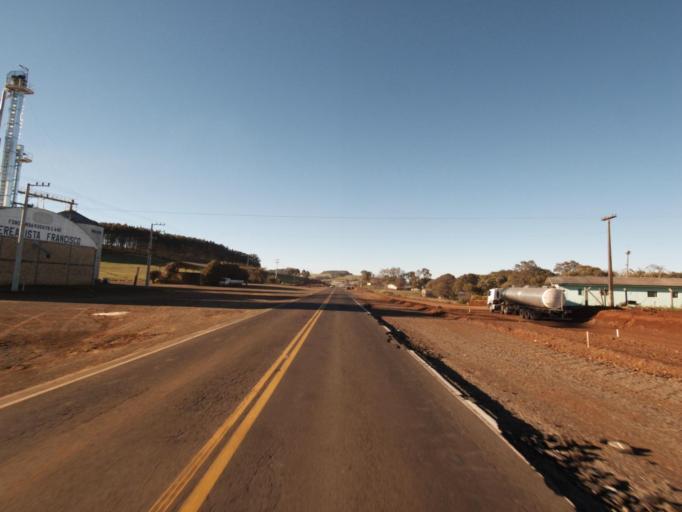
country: AR
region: Misiones
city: Bernardo de Irigoyen
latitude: -26.4221
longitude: -53.5254
